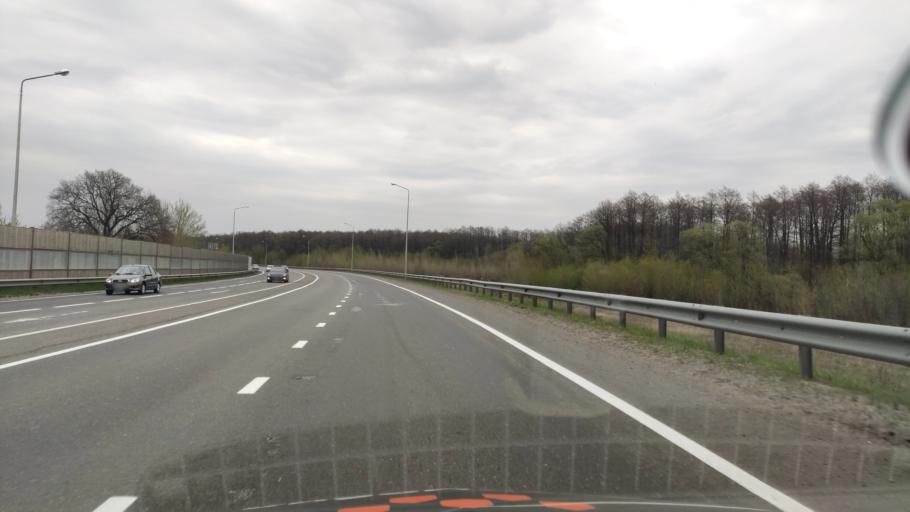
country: RU
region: Belgorod
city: Staryy Oskol
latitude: 51.3467
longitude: 37.8219
